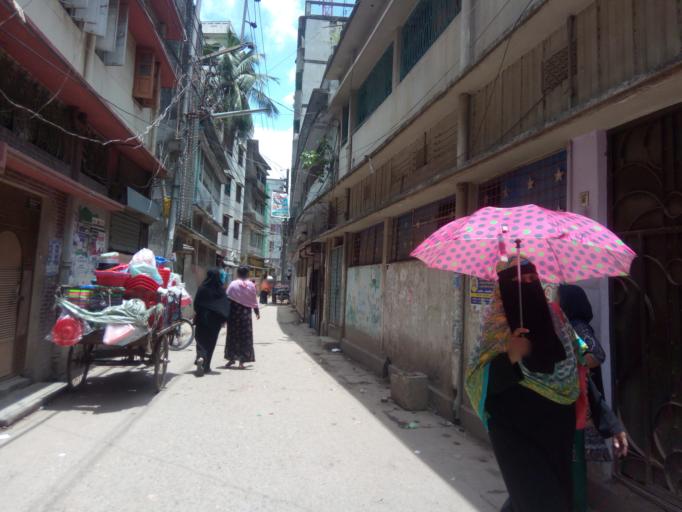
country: BD
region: Dhaka
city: Azimpur
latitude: 23.7288
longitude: 90.3716
